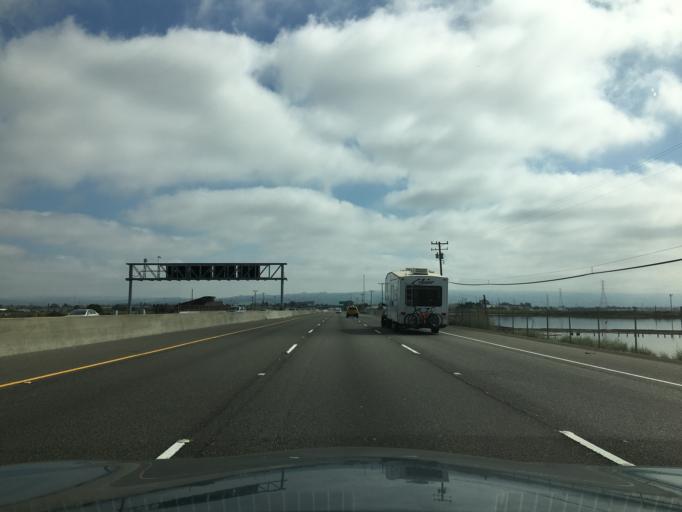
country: US
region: California
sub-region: Alameda County
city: San Lorenzo
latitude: 37.6216
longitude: -122.1402
